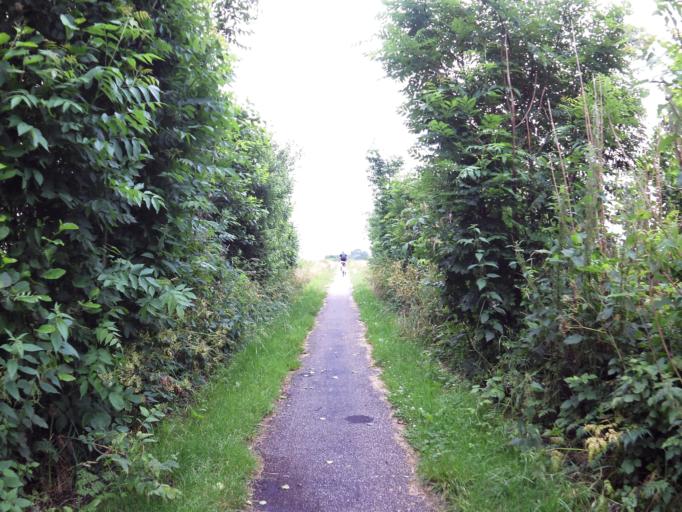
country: NL
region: Utrecht
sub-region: Stichtse Vecht
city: Breukelen
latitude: 52.1288
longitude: 4.9483
